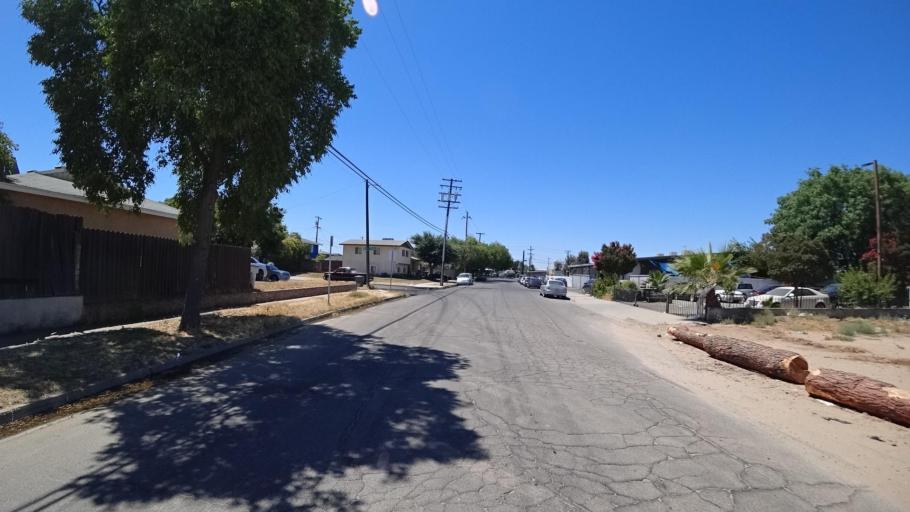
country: US
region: California
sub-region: Fresno County
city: Fresno
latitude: 36.8024
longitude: -119.7881
